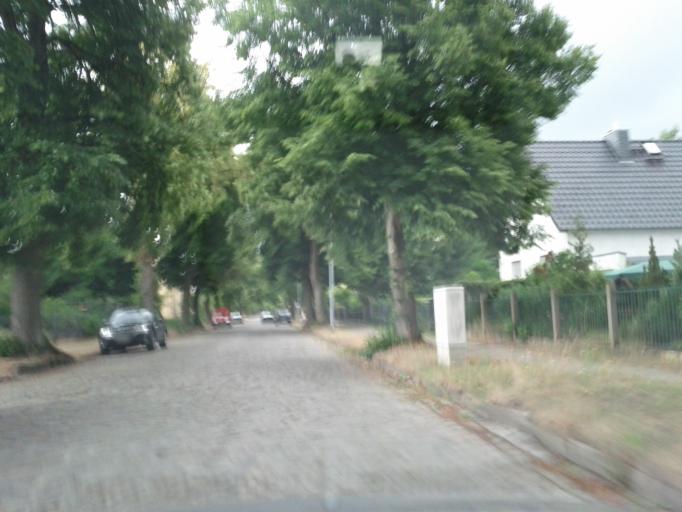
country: DE
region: Brandenburg
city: Schoneiche
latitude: 52.4715
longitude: 13.7099
